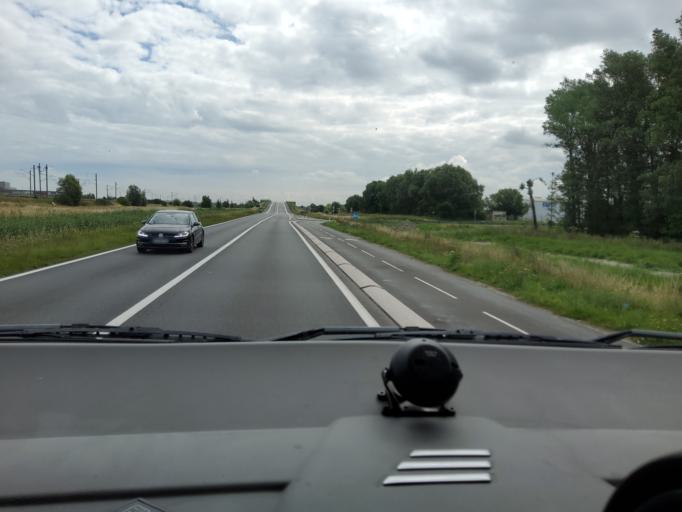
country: FR
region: Nord-Pas-de-Calais
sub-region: Departement du Nord
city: Gravelines
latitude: 50.9960
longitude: 2.1606
